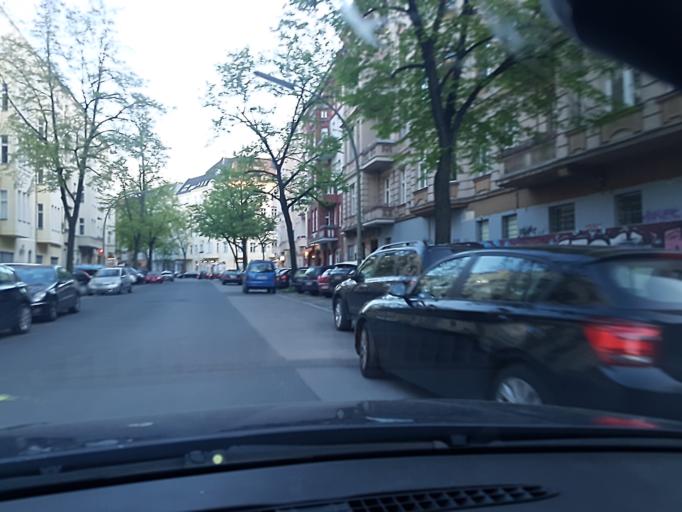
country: DE
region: Berlin
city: Berlin Schoeneberg
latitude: 52.4883
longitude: 13.3493
